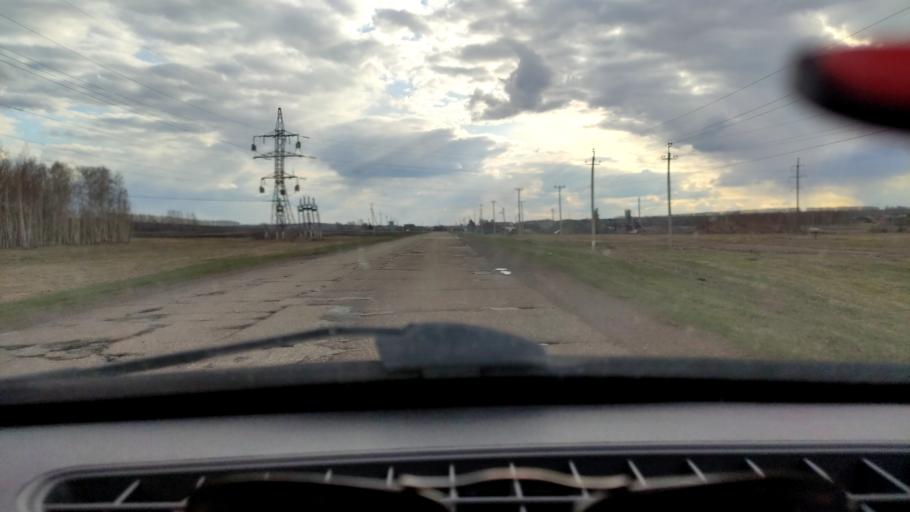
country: RU
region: Bashkortostan
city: Ulukulevo
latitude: 54.4077
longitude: 56.2593
